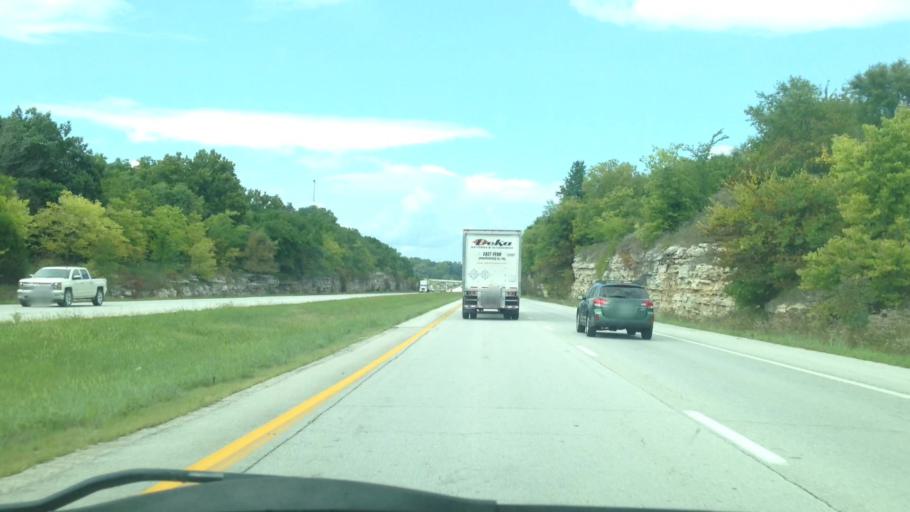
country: US
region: Missouri
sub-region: Marion County
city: Palmyra
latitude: 39.8026
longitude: -91.5163
